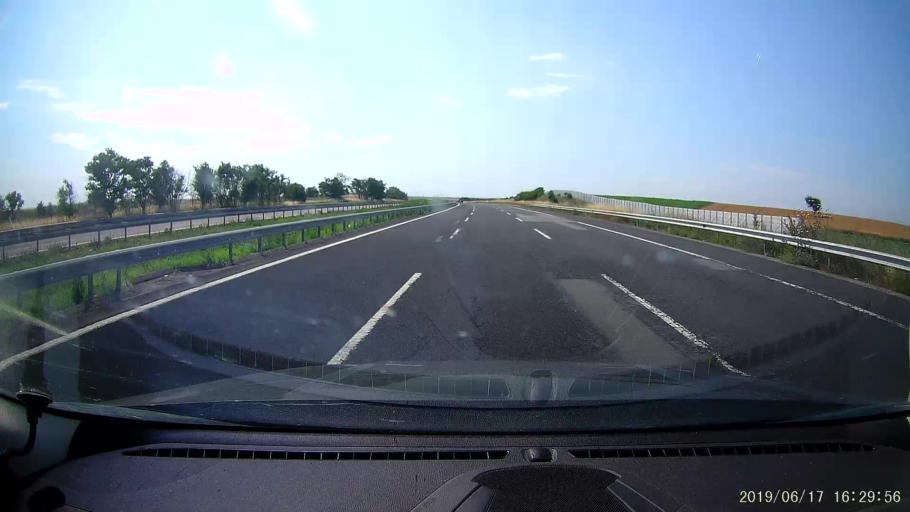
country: TR
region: Tekirdag
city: Beyazkoy
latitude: 41.3402
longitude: 27.6685
